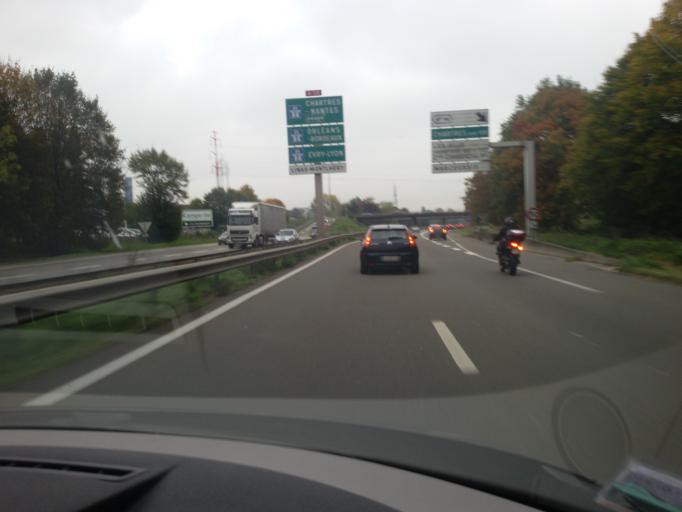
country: FR
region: Ile-de-France
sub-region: Departement de l'Essonne
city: Orsay
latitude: 48.6786
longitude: 2.1919
